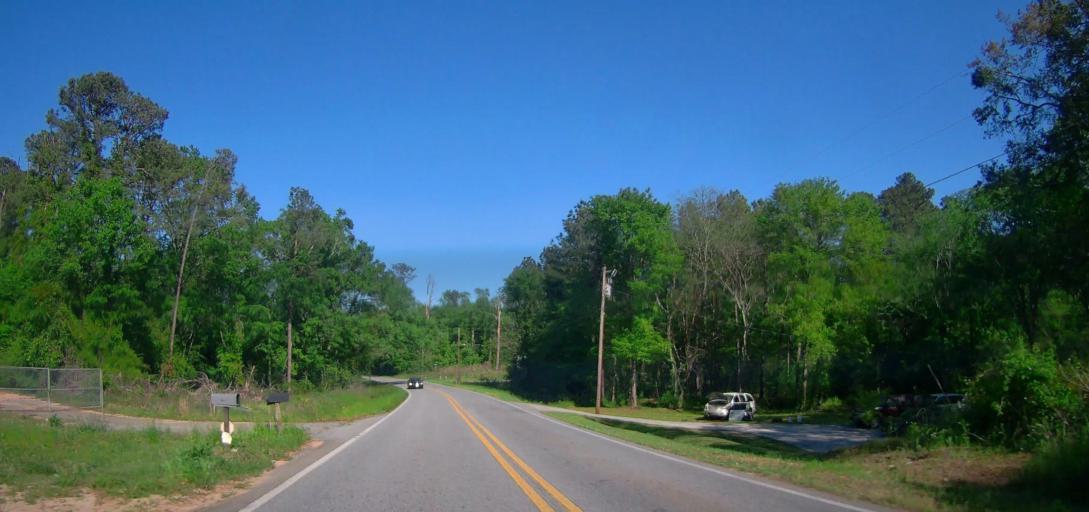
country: US
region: Georgia
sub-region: Houston County
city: Warner Robins
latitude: 32.6567
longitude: -83.6286
